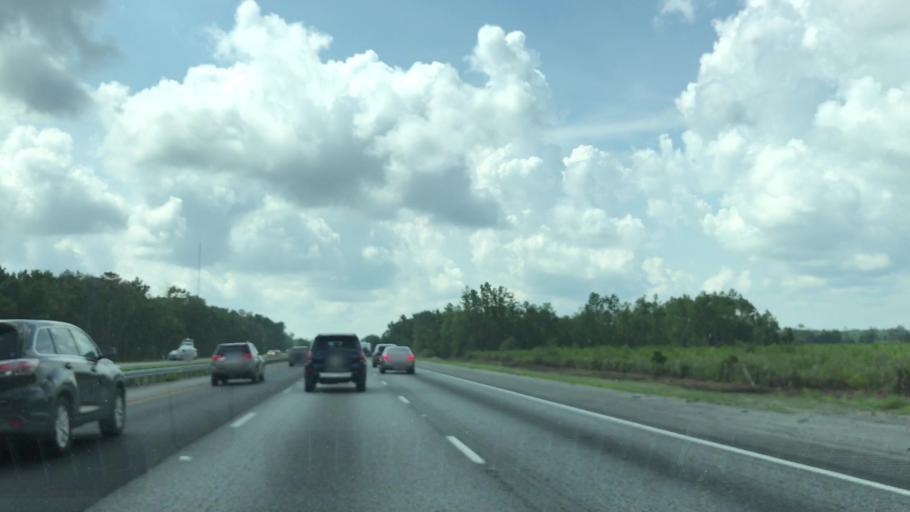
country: US
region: Georgia
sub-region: Camden County
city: Kingsland
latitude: 30.8636
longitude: -81.6805
